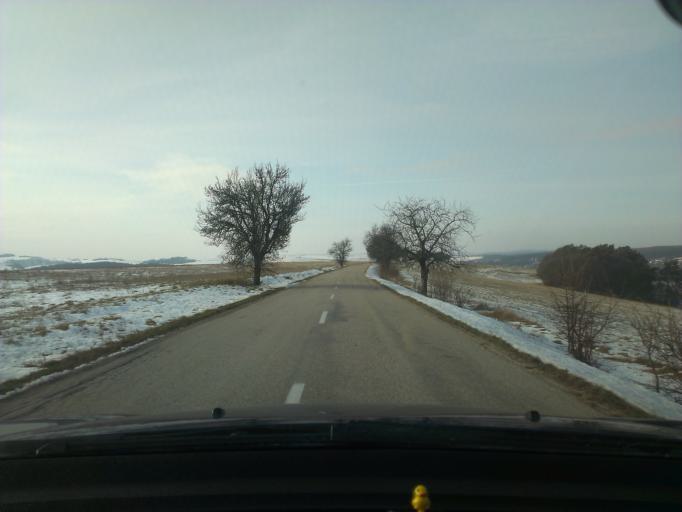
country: SK
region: Nitriansky
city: Stara Tura
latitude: 48.7447
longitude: 17.6439
